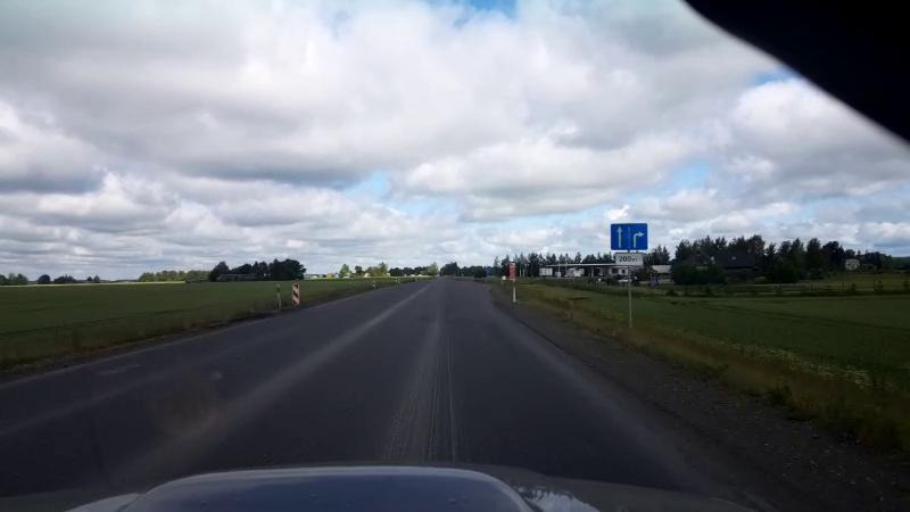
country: LV
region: Bauskas Rajons
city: Bauska
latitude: 56.3139
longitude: 24.3310
